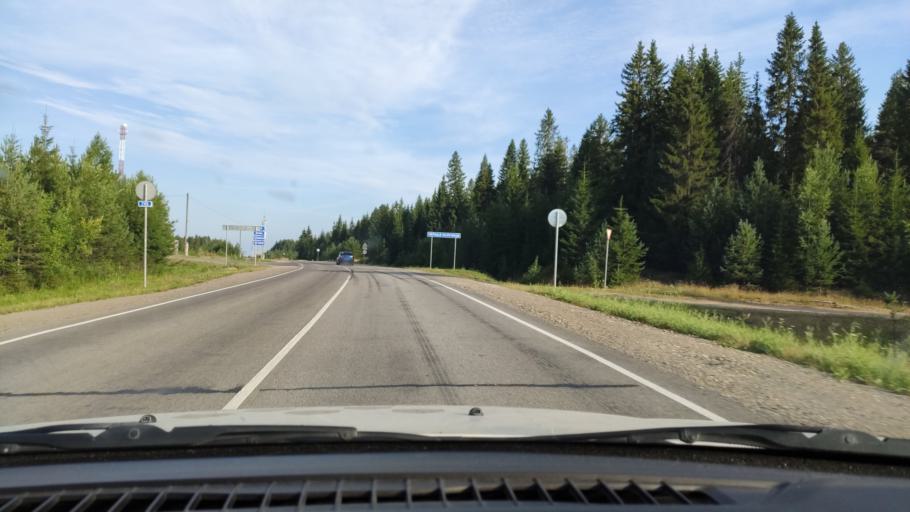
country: RU
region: Kirov
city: Chernaya Kholunitsa
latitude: 58.8524
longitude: 51.7374
